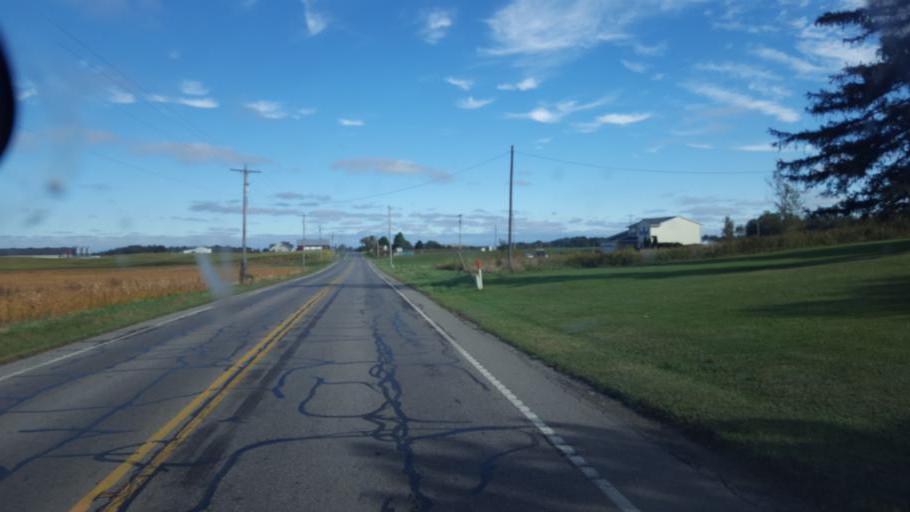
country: US
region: Ohio
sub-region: Huron County
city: Greenwich
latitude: 40.9299
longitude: -82.4964
